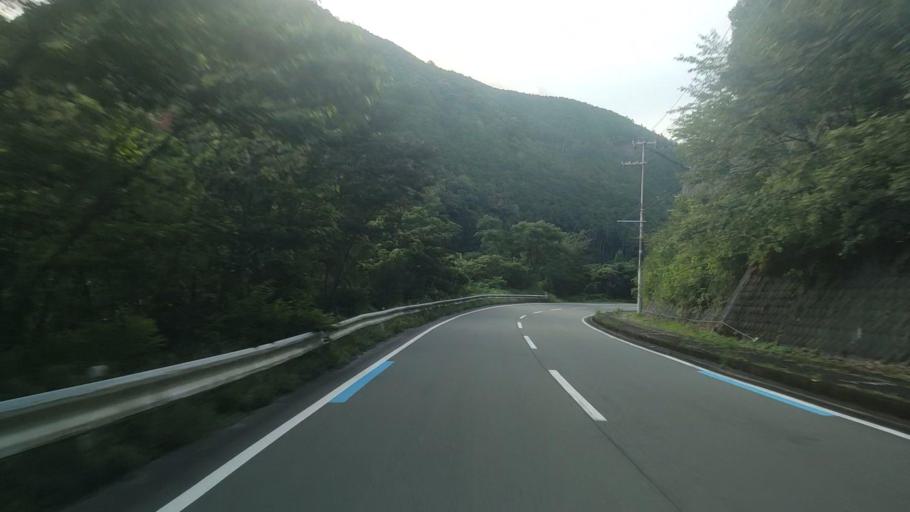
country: JP
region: Wakayama
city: Shingu
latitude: 33.8191
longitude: 135.7679
